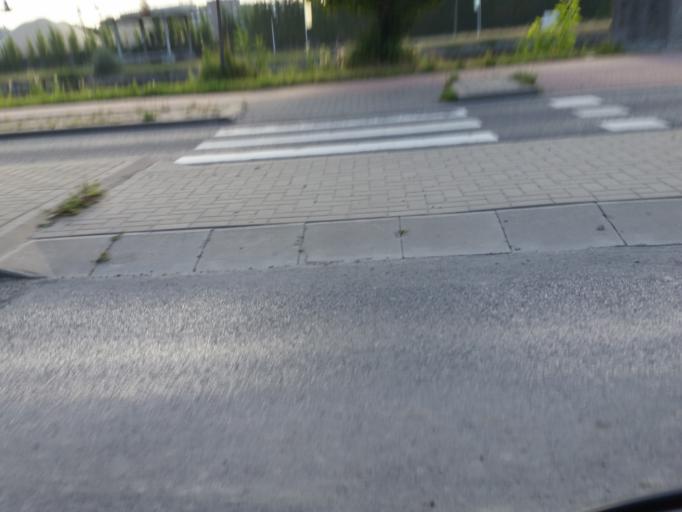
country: BE
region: Flanders
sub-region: Provincie Vlaams-Brabant
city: Vilvoorde
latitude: 50.9213
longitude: 4.4187
